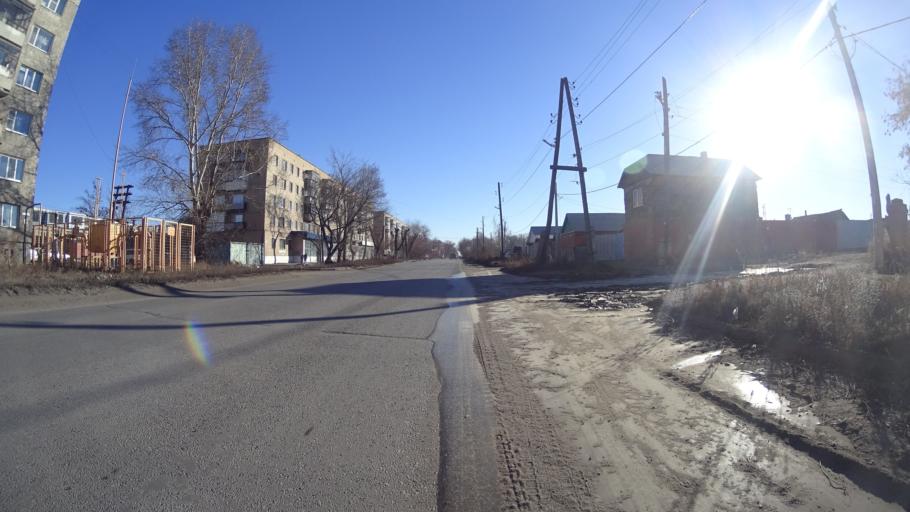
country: RU
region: Chelyabinsk
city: Troitsk
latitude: 54.1151
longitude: 61.5640
